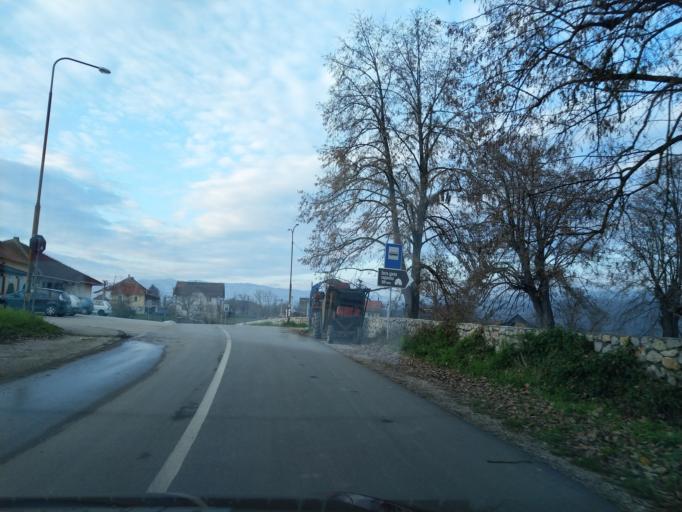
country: RS
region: Central Serbia
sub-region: Zlatiborski Okrug
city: Kosjeric
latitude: 43.9159
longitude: 19.9112
